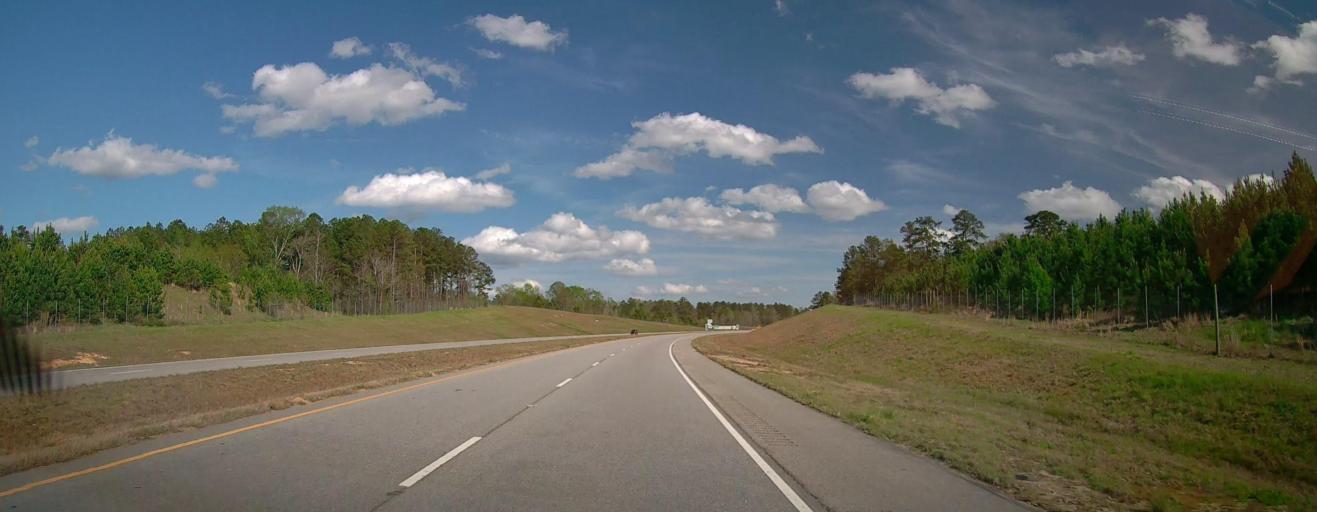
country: US
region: Georgia
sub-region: Baldwin County
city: Hardwick
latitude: 33.0409
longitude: -83.1223
